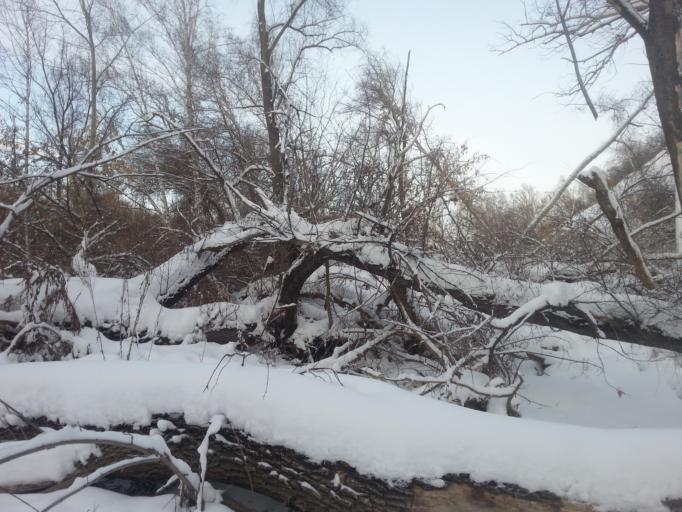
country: RU
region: Altai Krai
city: Nauchnyy Gorodok
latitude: 53.4265
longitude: 83.5053
